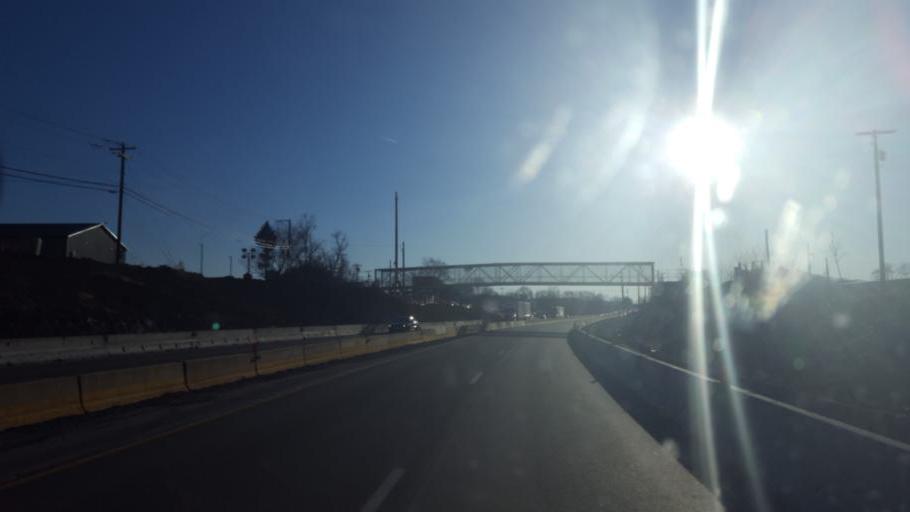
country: US
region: Pennsylvania
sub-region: Westmoreland County
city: New Stanton
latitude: 40.2190
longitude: -79.6034
